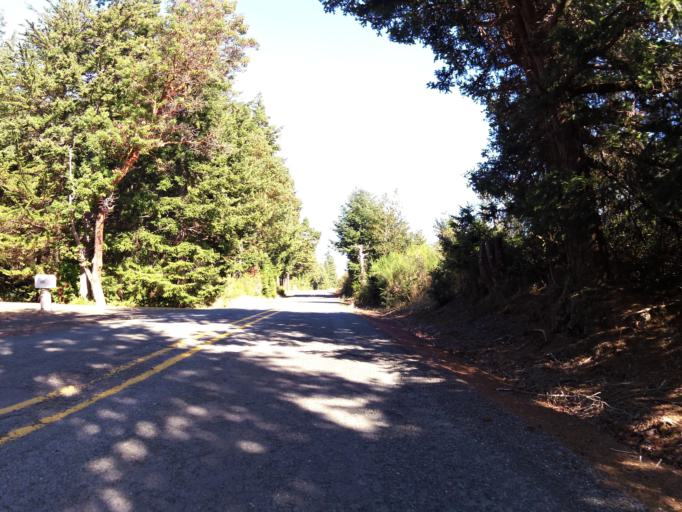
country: US
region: Oregon
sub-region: Coos County
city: Bandon
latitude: 43.0397
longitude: -124.4107
